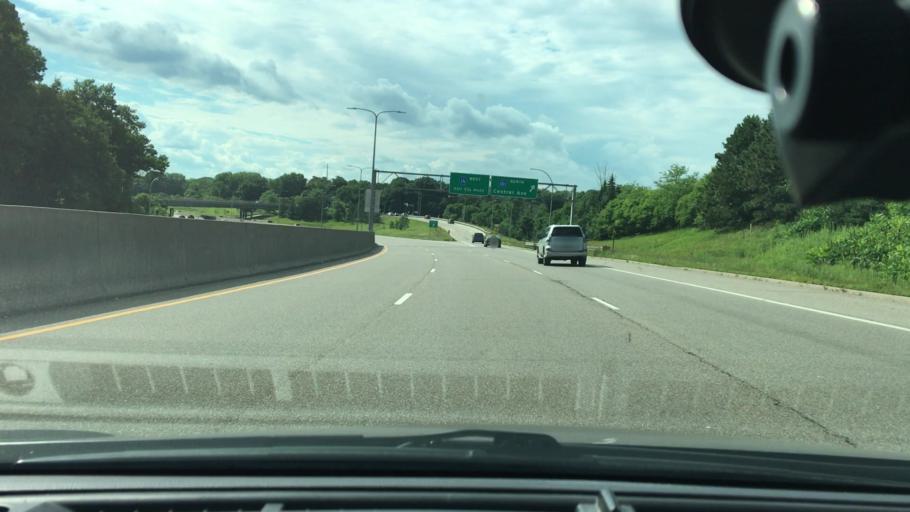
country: US
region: Minnesota
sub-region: Hennepin County
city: Wayzata
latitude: 44.9746
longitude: -93.4974
